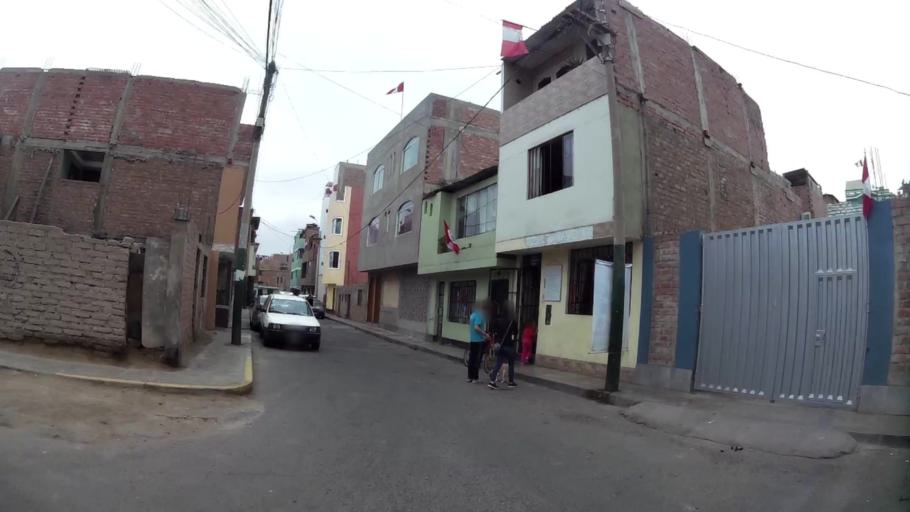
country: PE
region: Lima
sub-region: Lima
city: Surco
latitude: -12.1542
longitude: -77.0157
